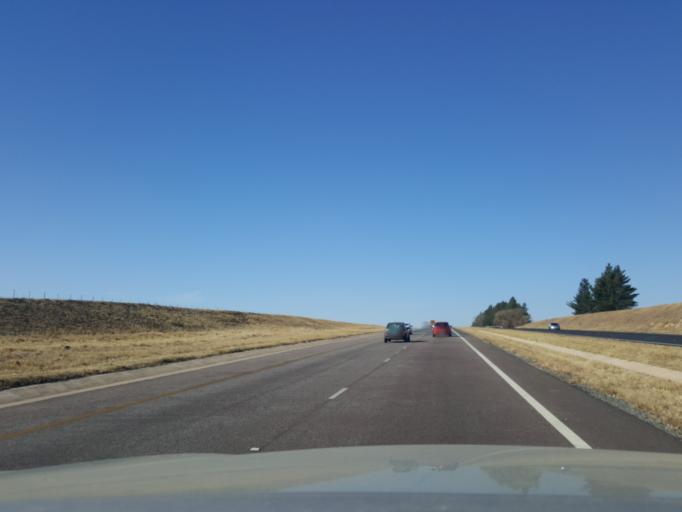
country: ZA
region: Mpumalanga
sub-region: Nkangala District Municipality
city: Belfast
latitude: -25.8225
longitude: 29.8536
